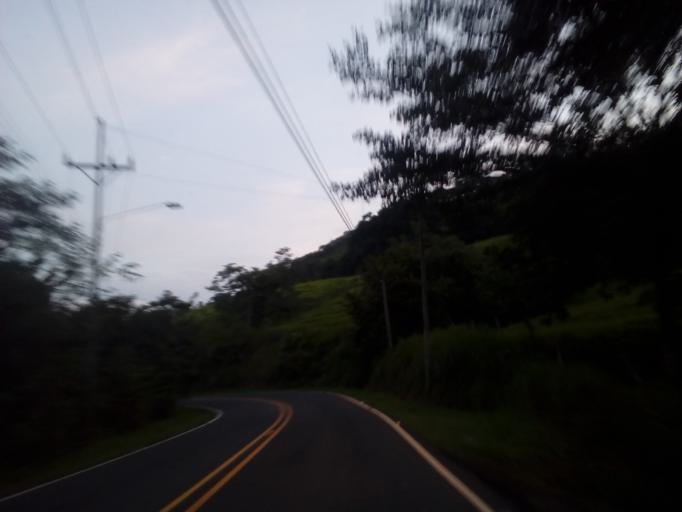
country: CR
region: Guanacaste
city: Hojancha
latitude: 10.0151
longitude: -85.5008
